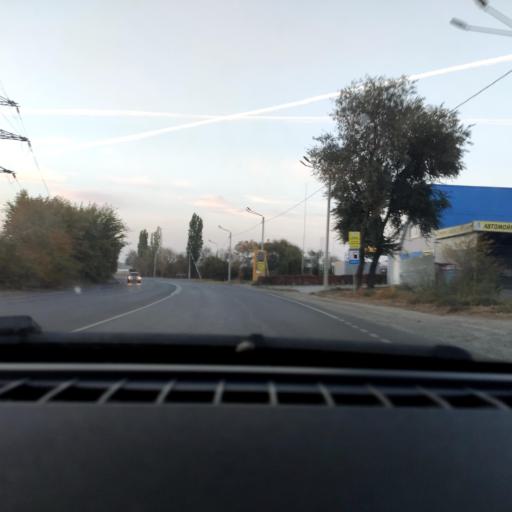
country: RU
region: Voronezj
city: Maslovka
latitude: 51.6310
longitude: 39.2869
